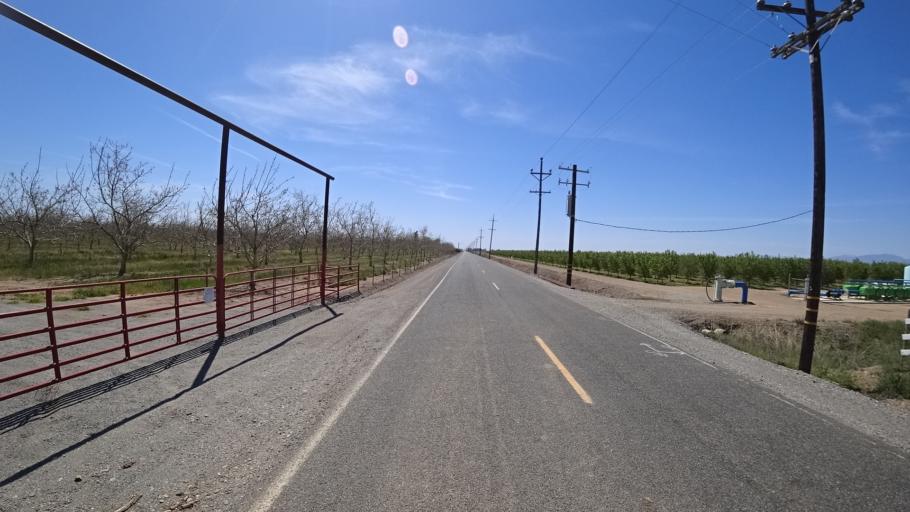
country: US
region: California
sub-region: Glenn County
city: Orland
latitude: 39.6894
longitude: -122.1780
